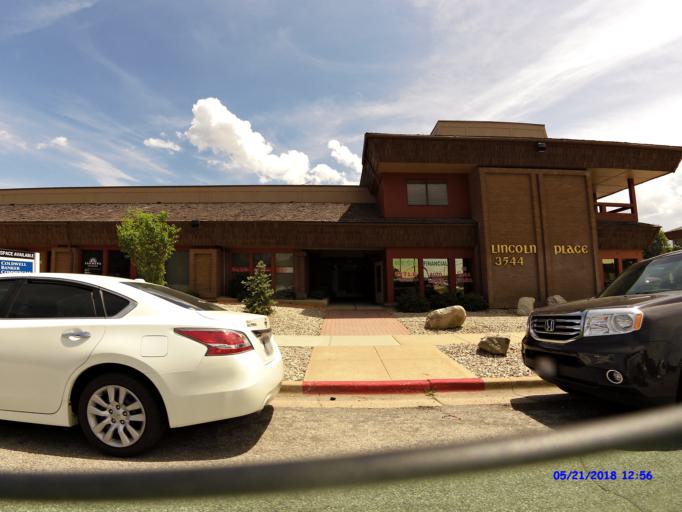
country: US
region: Utah
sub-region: Weber County
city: South Ogden
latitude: 41.1990
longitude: -111.9766
